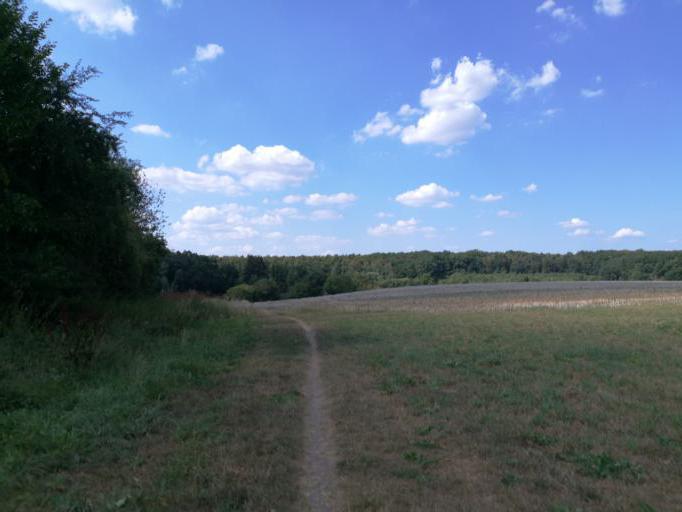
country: DE
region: Bavaria
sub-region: Regierungsbezirk Mittelfranken
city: Seukendorf
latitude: 49.4818
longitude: 10.9083
